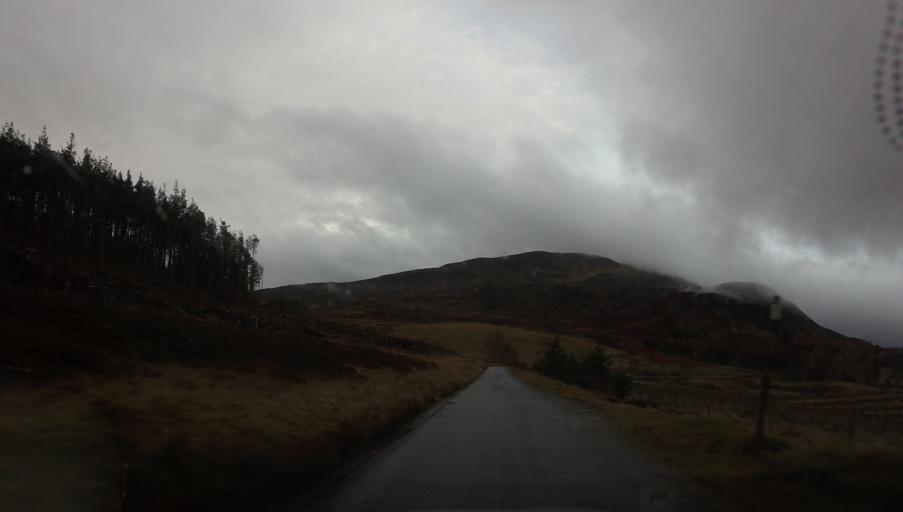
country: GB
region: Scotland
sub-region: Perth and Kinross
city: Aberfeldy
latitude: 56.6778
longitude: -4.0343
